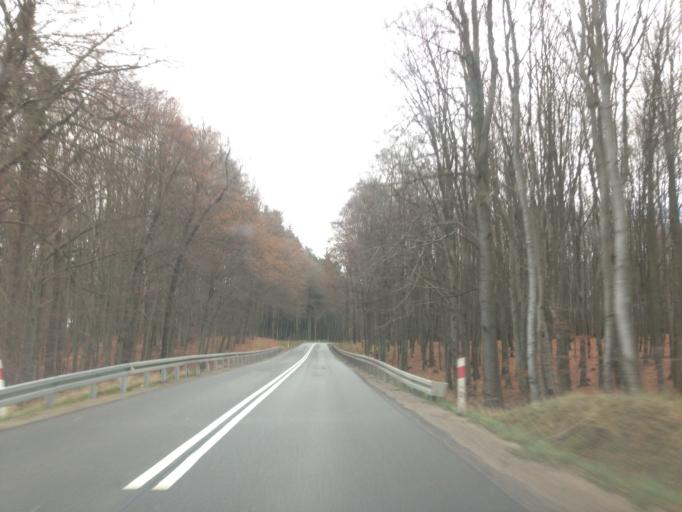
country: PL
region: Pomeranian Voivodeship
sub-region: Powiat gdanski
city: Kolbudy
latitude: 54.2503
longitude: 18.3906
